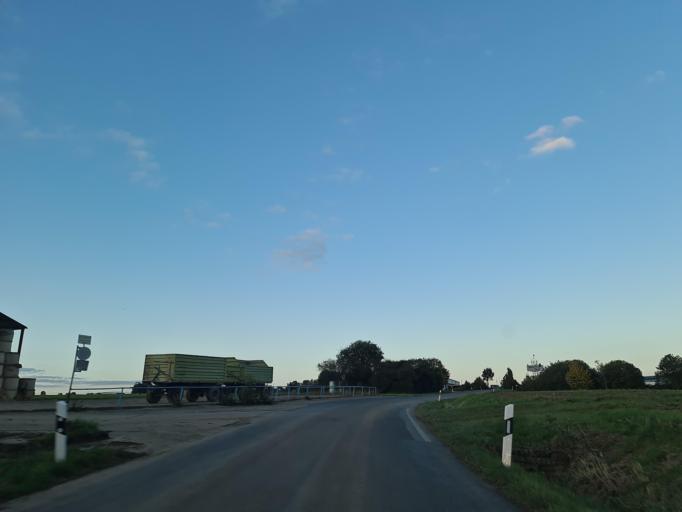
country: DE
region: Saxony
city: Syrau
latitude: 50.5298
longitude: 12.0979
